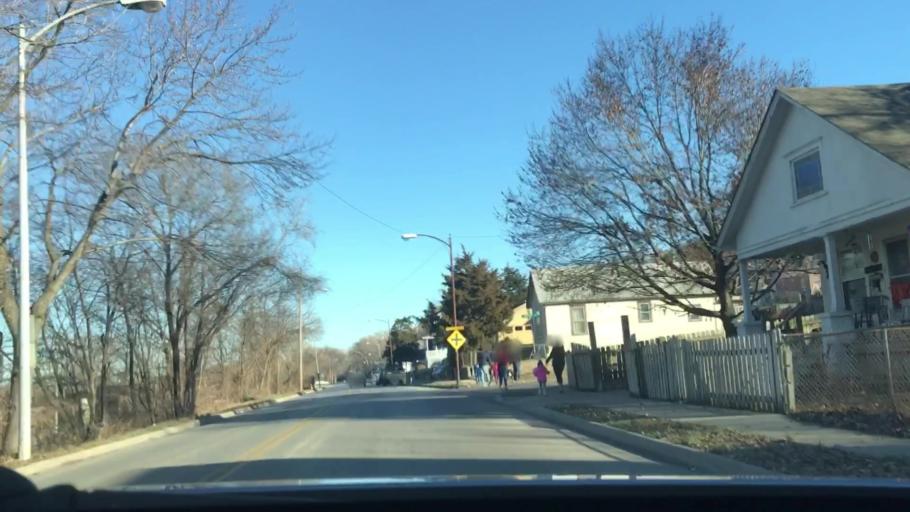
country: US
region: Kansas
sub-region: Johnson County
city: Roeland Park
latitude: 39.0722
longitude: -94.6423
